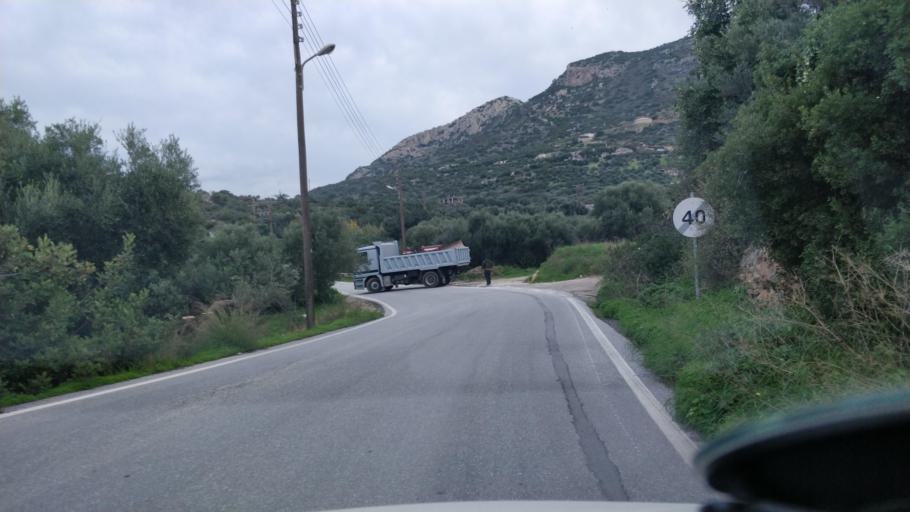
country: GR
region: Crete
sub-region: Nomos Lasithiou
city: Agios Nikolaos
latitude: 35.1170
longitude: 25.7266
